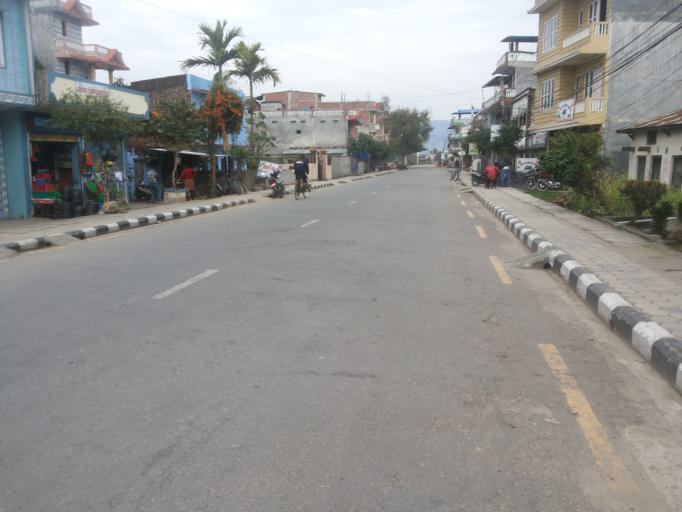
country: NP
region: Central Region
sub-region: Narayani Zone
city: Bharatpur
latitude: 27.6905
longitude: 84.4362
